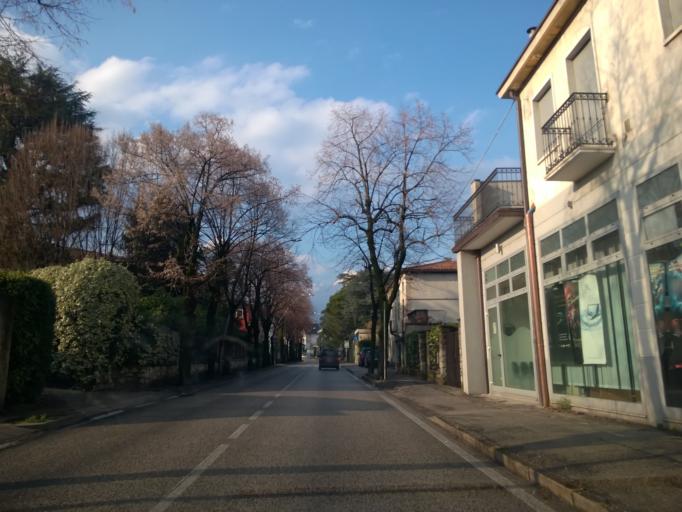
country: IT
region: Veneto
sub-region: Provincia di Vicenza
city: Thiene
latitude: 45.7029
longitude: 11.4753
